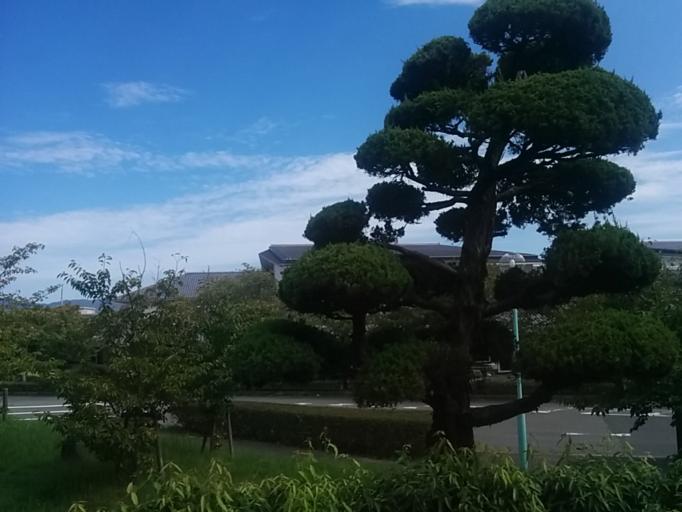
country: JP
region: Nara
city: Nara-shi
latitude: 34.6525
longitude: 135.7817
